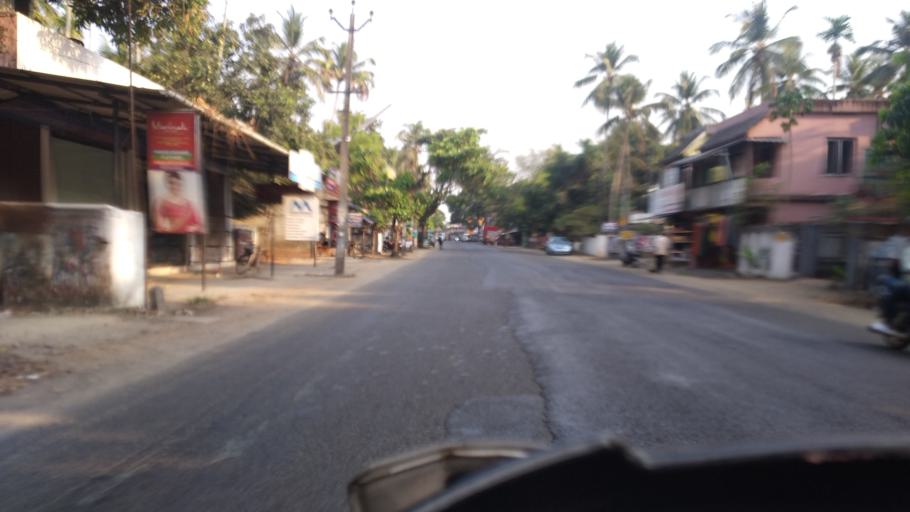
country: IN
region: Kerala
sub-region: Thrissur District
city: Thanniyam
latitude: 10.4067
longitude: 76.1106
